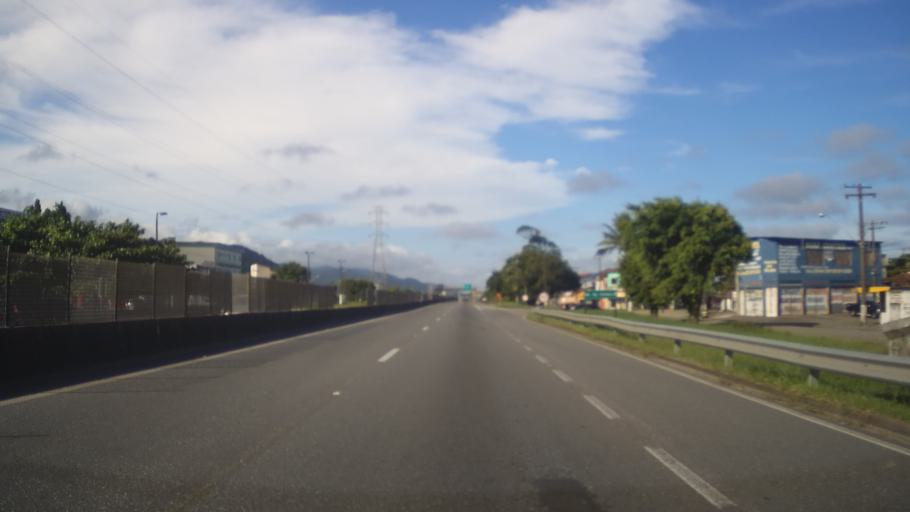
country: BR
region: Sao Paulo
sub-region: Mongagua
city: Mongagua
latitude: -24.1291
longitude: -46.6910
